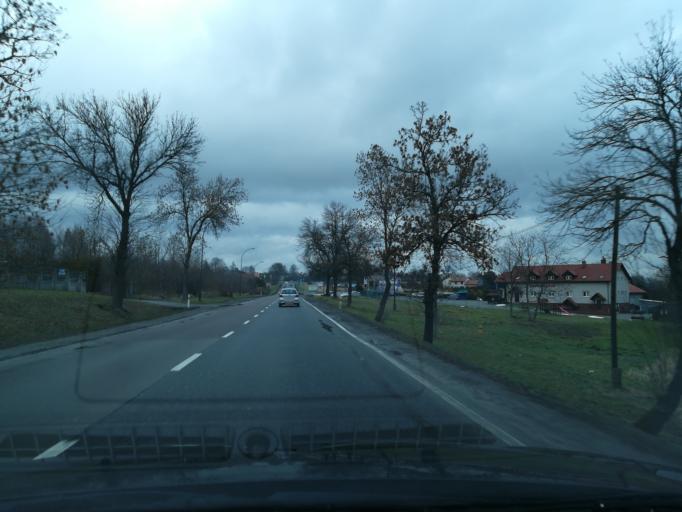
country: PL
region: Subcarpathian Voivodeship
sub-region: Powiat lancucki
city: Lancut
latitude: 50.0695
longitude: 22.2462
